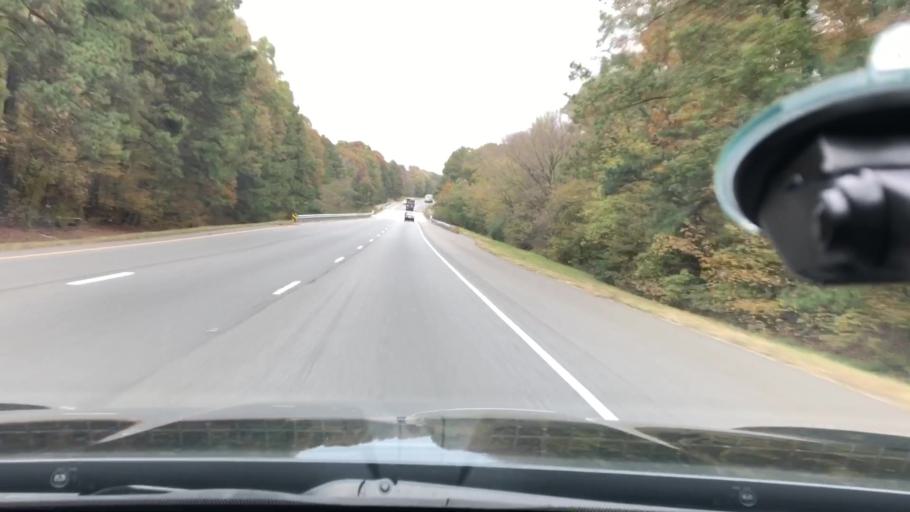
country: US
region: Arkansas
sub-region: Hot Spring County
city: Malvern
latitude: 34.3524
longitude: -92.8864
